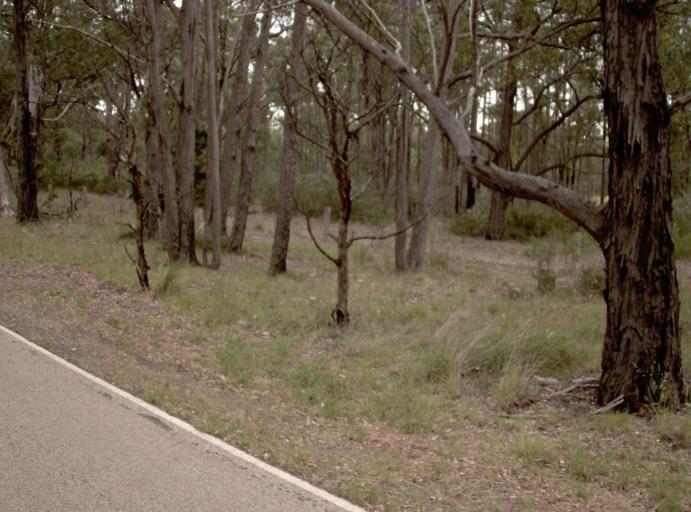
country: AU
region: Victoria
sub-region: East Gippsland
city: Bairnsdale
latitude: -37.7447
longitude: 147.3152
